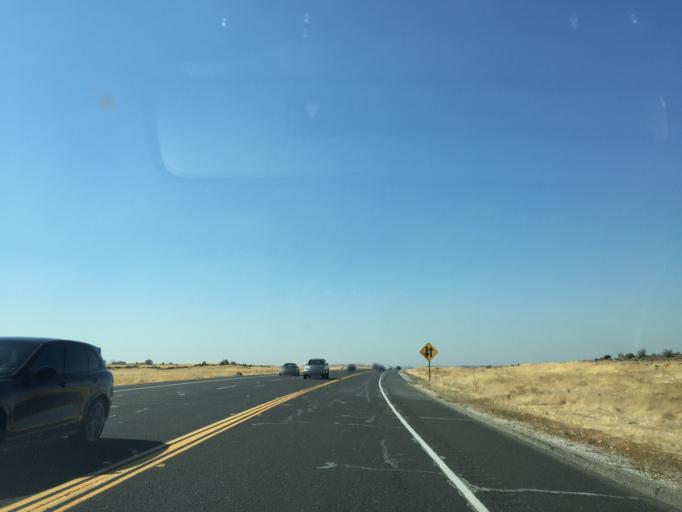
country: US
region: California
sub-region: Calaveras County
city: Copperopolis
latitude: 37.8222
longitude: -120.6425
